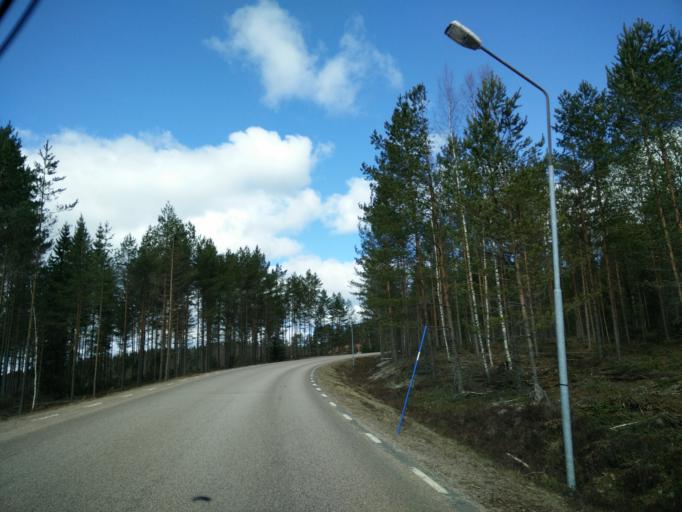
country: SE
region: Vaermland
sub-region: Hagfors Kommun
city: Hagfors
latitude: 59.8849
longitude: 13.7135
